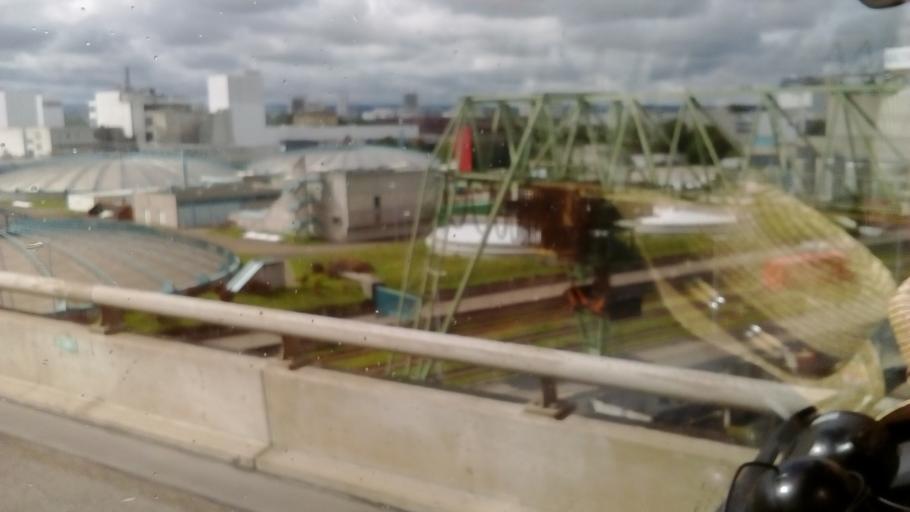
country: DE
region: Baden-Wuerttemberg
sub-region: Freiburg Region
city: Weil am Rhein
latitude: 47.5839
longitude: 7.6017
